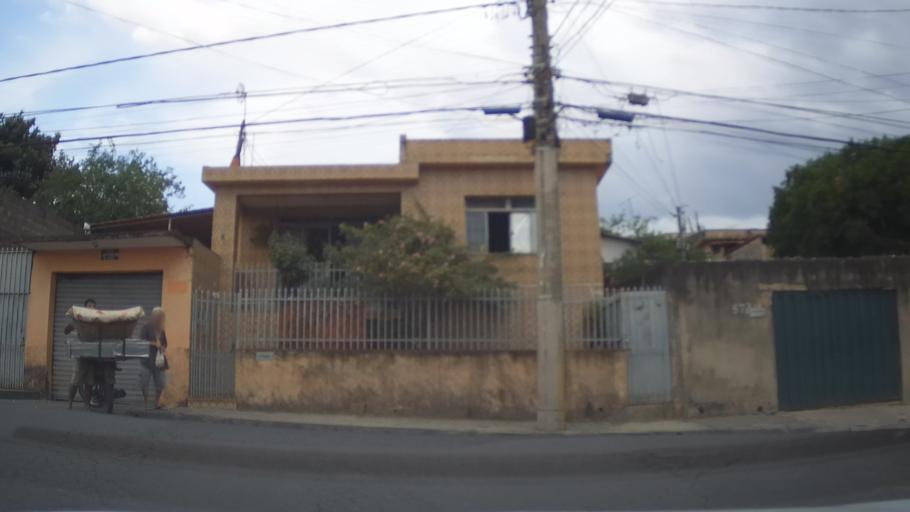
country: BR
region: Minas Gerais
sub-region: Belo Horizonte
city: Belo Horizonte
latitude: -19.8769
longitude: -43.9232
